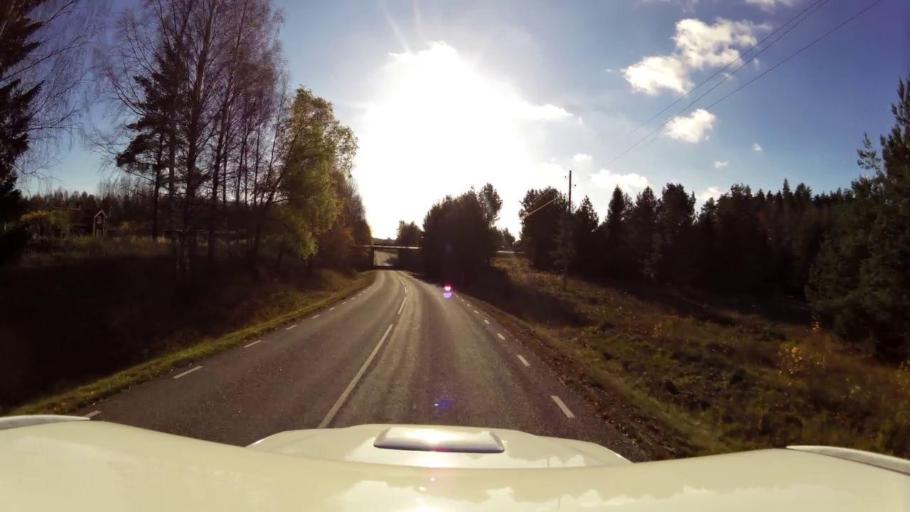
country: SE
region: OEstergoetland
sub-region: Linkopings Kommun
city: Linghem
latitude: 58.4564
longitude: 15.7749
